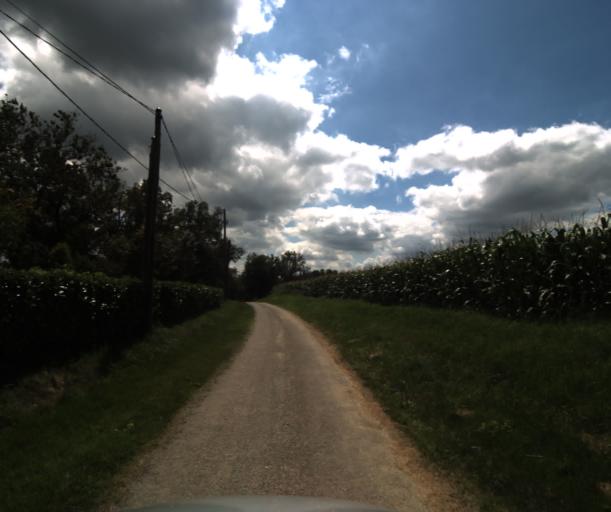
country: FR
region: Midi-Pyrenees
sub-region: Departement de la Haute-Garonne
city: Lacasse
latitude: 43.4081
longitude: 1.2720
